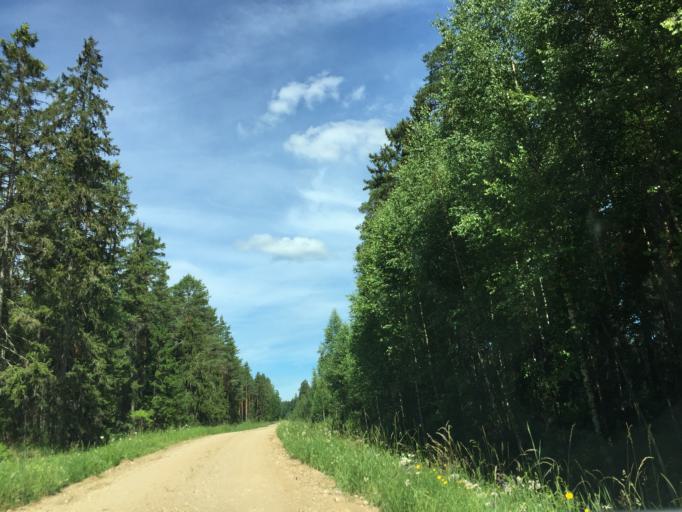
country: LV
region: Dundaga
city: Dundaga
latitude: 57.4209
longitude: 22.0827
